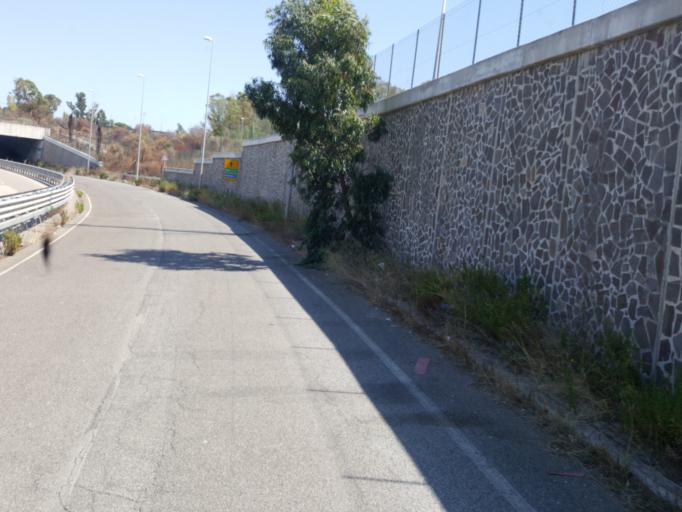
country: IT
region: Latium
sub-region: Citta metropolitana di Roma Capitale
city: Aurelia
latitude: 42.1251
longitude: 11.7836
